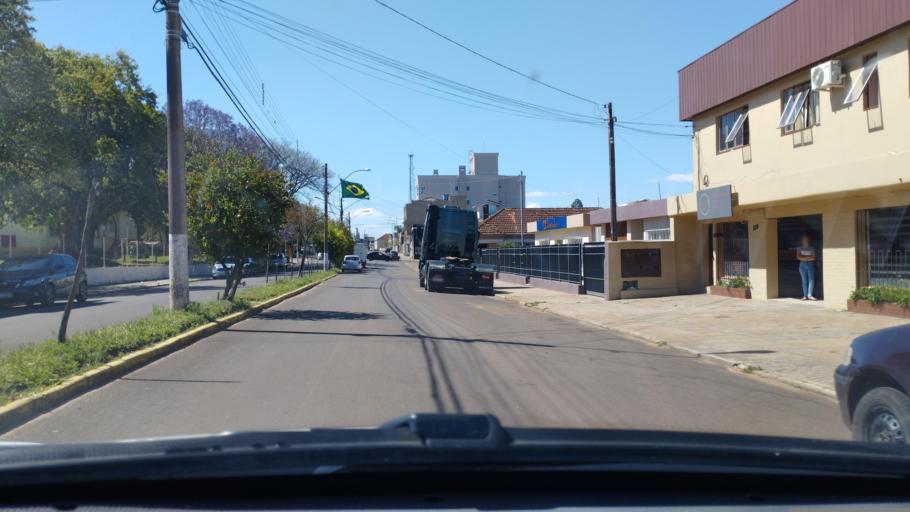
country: BR
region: Rio Grande do Sul
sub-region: Tupancireta
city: Tupancireta
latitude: -29.0866
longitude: -53.8351
